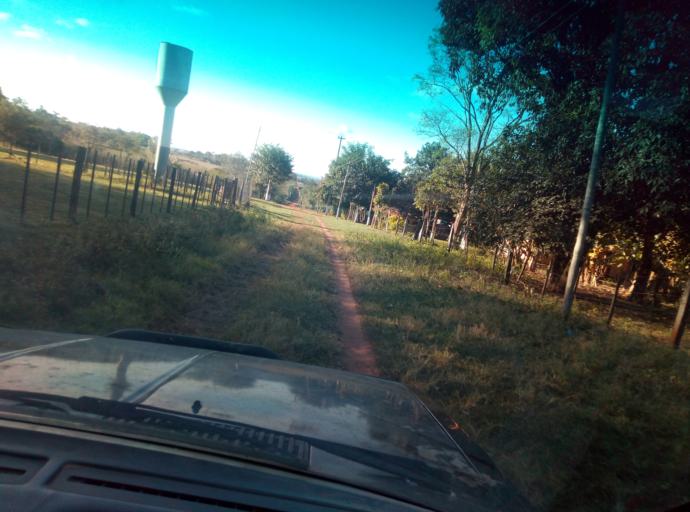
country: PY
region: Caaguazu
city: Carayao
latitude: -25.1814
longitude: -56.2647
